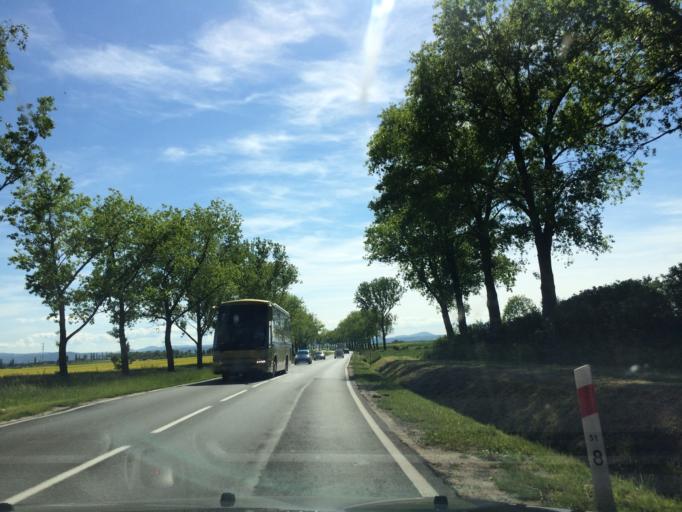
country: PL
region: Lower Silesian Voivodeship
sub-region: Powiat swidnicki
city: Swidnica
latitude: 50.8739
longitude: 16.5728
